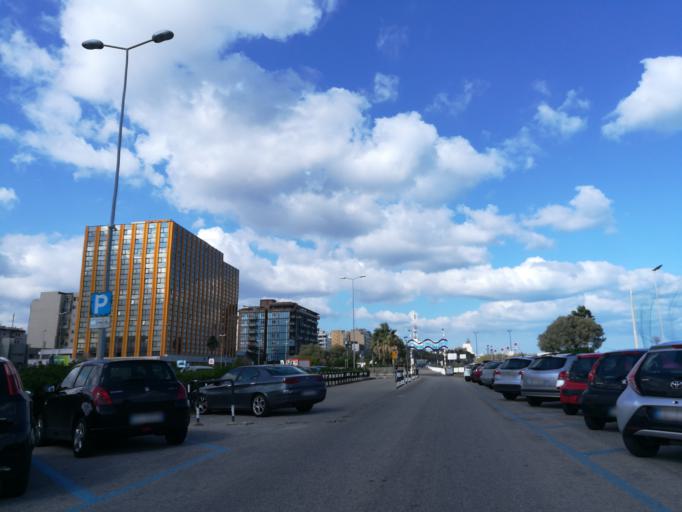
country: IT
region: Apulia
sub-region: Provincia di Bari
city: Bari
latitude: 41.1170
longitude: 16.8962
